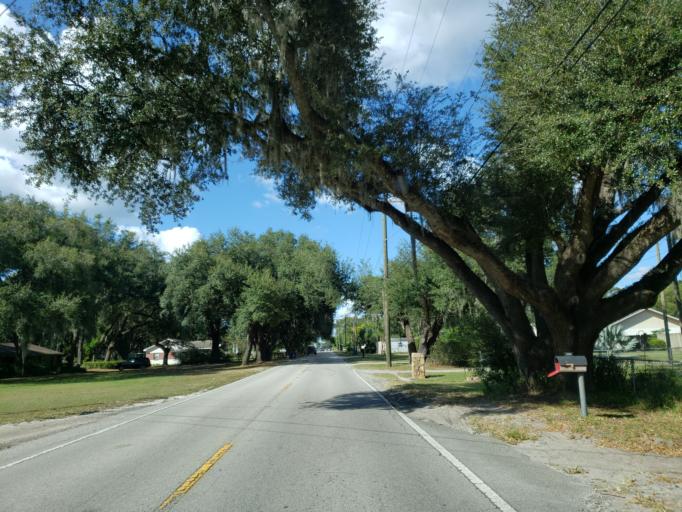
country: US
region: Florida
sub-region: Hillsborough County
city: Dover
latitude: 27.9971
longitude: -82.1868
